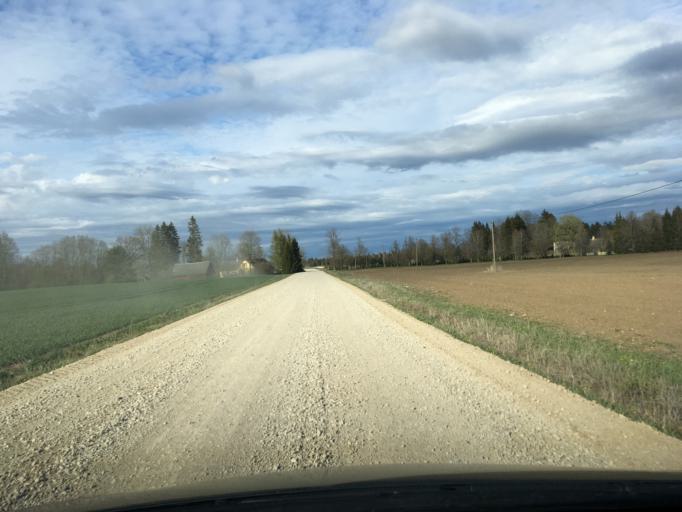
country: EE
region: Raplamaa
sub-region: Maerjamaa vald
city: Marjamaa
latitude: 58.9759
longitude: 24.3526
